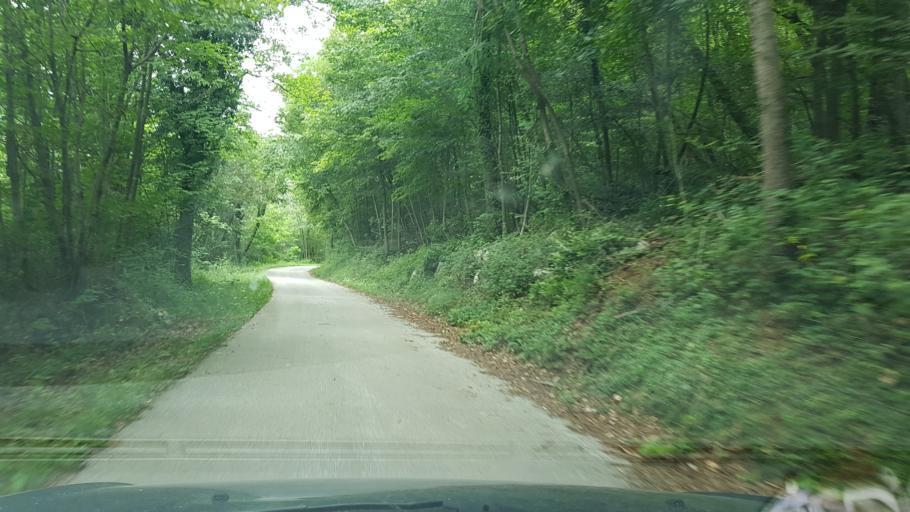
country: SI
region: Kanal
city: Deskle
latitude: 46.0269
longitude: 13.6128
